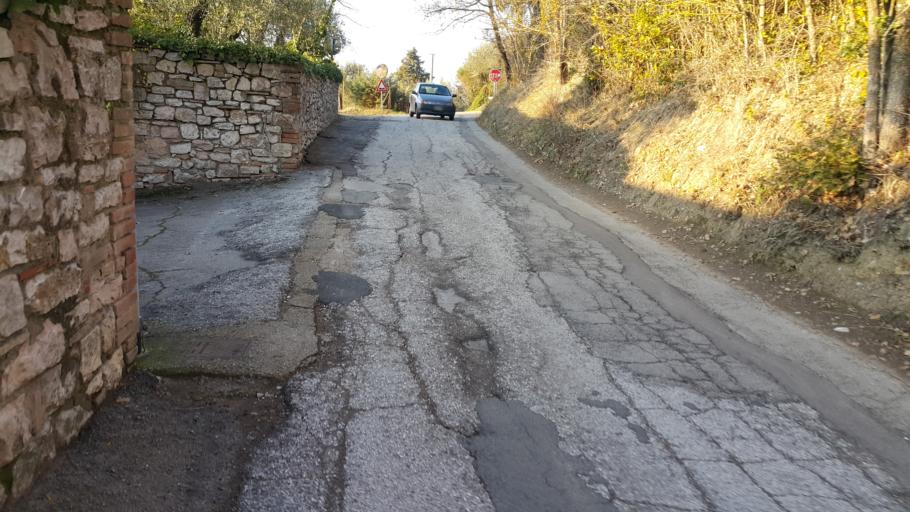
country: IT
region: Umbria
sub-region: Provincia di Perugia
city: Perugia
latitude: 43.0887
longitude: 12.3774
